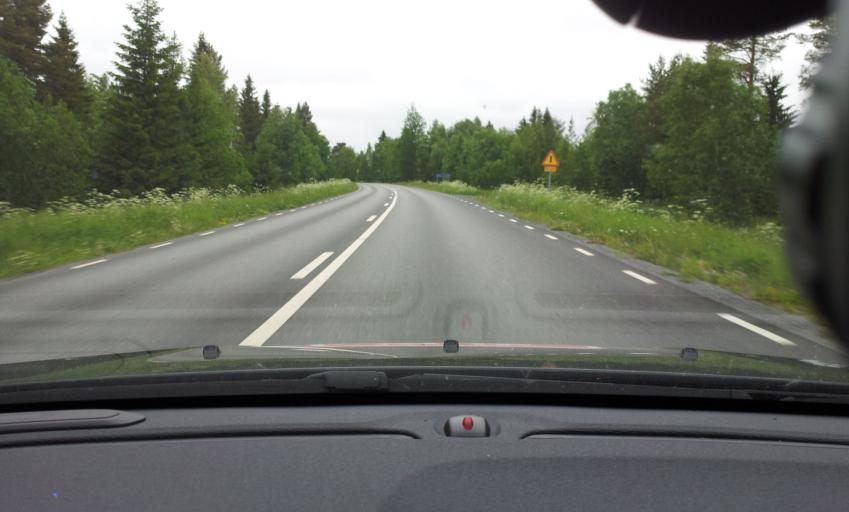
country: SE
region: Jaemtland
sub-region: Krokoms Kommun
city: Krokom
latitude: 63.0961
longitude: 14.3030
